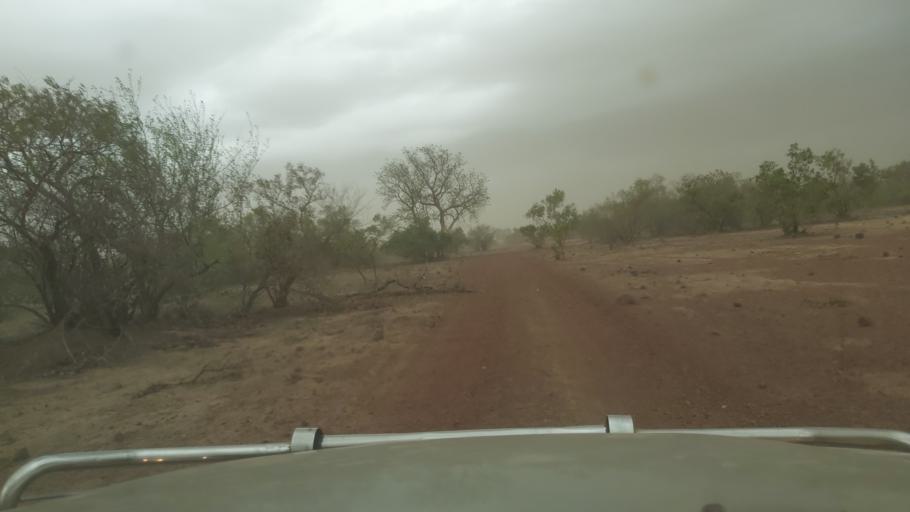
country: ML
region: Koulikoro
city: Banamba
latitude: 13.3651
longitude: -7.1847
